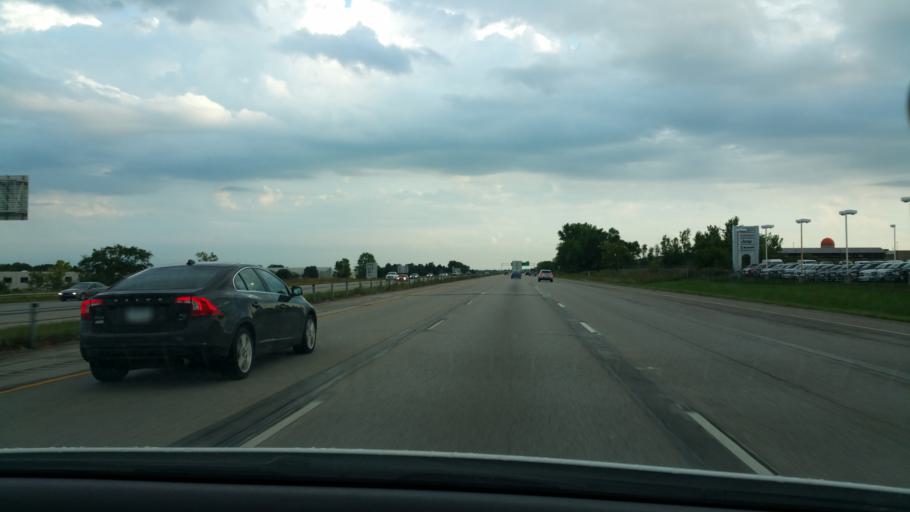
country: US
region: Iowa
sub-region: Polk County
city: Ankeny
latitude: 41.6987
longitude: -93.5762
